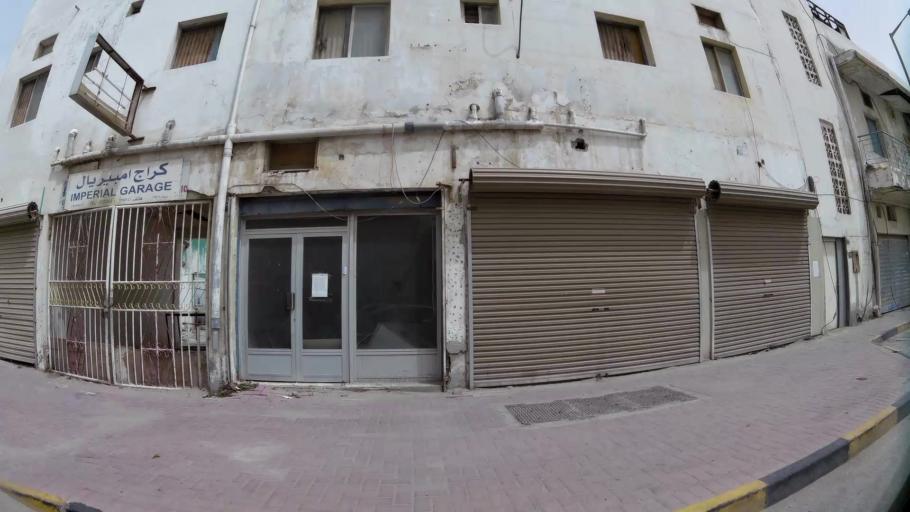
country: BH
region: Northern
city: Madinat `Isa
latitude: 26.1859
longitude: 50.5415
